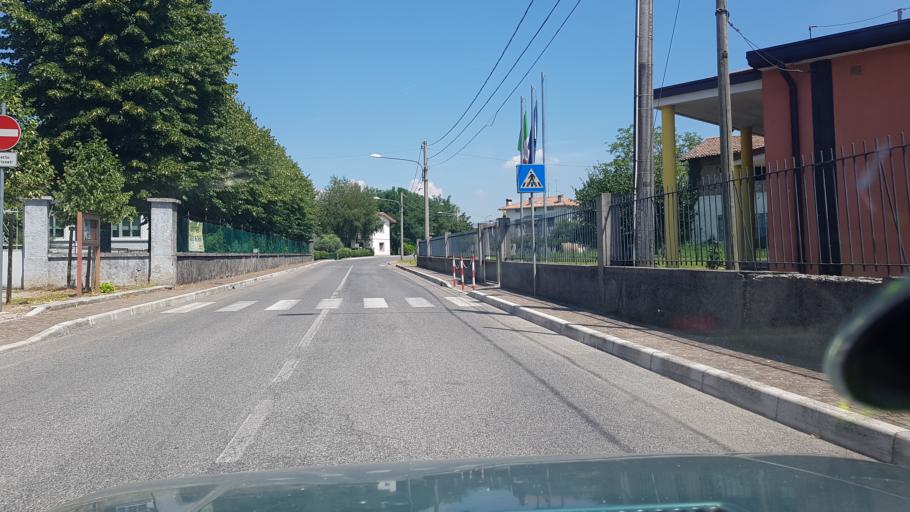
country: IT
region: Friuli Venezia Giulia
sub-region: Provincia di Gorizia
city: Moraro
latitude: 45.9316
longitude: 13.4986
